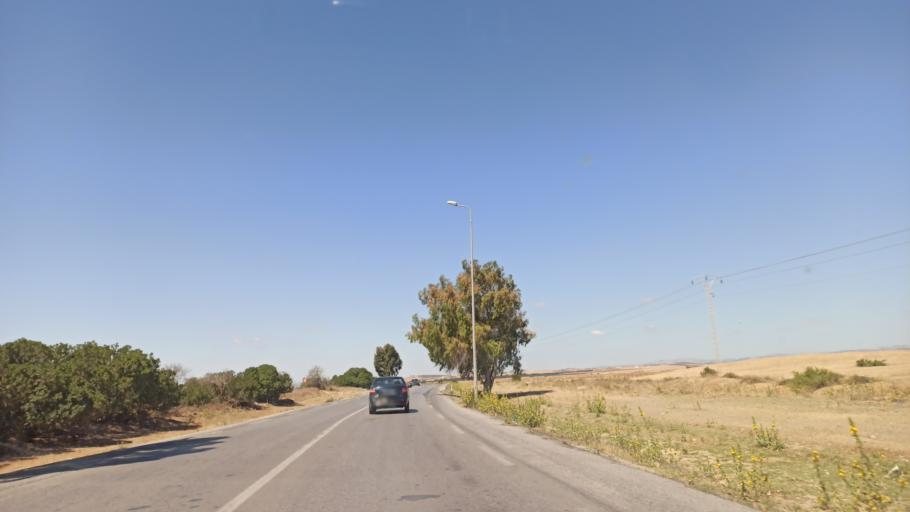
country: TN
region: Tunis
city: Oued Lill
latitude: 36.7473
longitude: 9.9695
